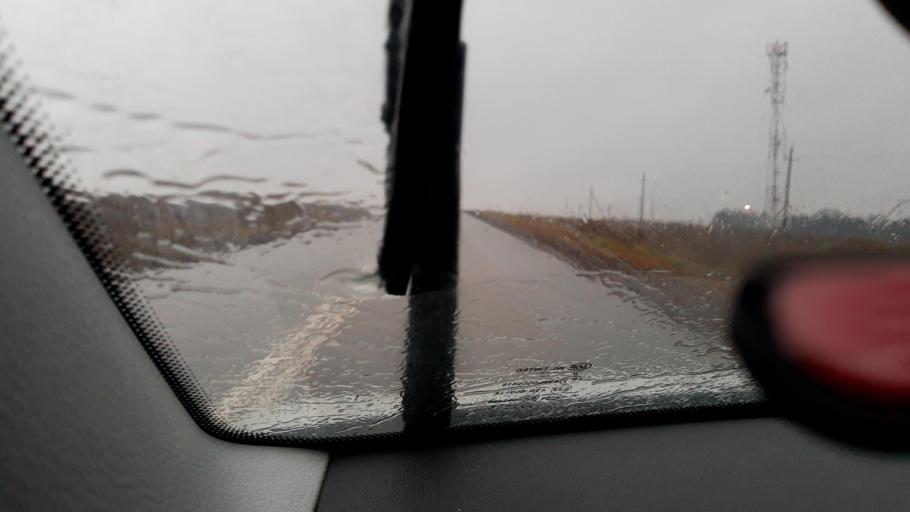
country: RU
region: Bashkortostan
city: Iglino
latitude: 54.9008
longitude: 56.1808
